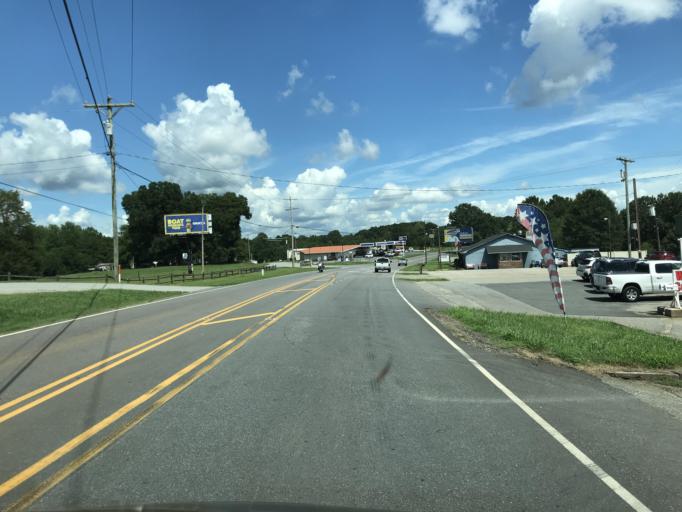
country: US
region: North Carolina
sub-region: Catawba County
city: Lake Norman of Catawba
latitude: 35.5726
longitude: -81.0396
